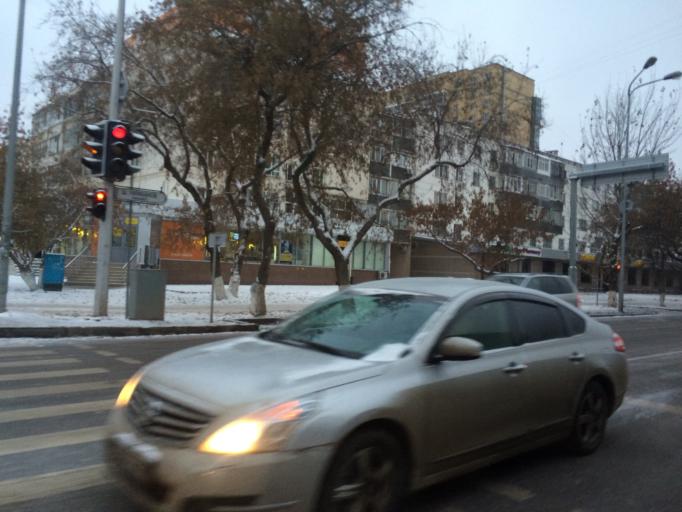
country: KZ
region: Astana Qalasy
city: Astana
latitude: 51.1700
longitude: 71.4391
